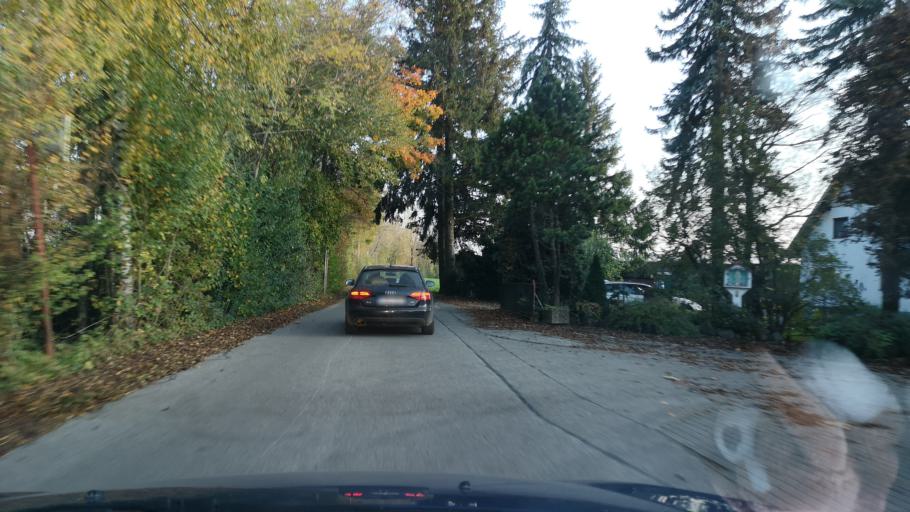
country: DE
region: Bavaria
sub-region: Upper Bavaria
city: Eichenried
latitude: 48.2346
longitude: 11.7546
